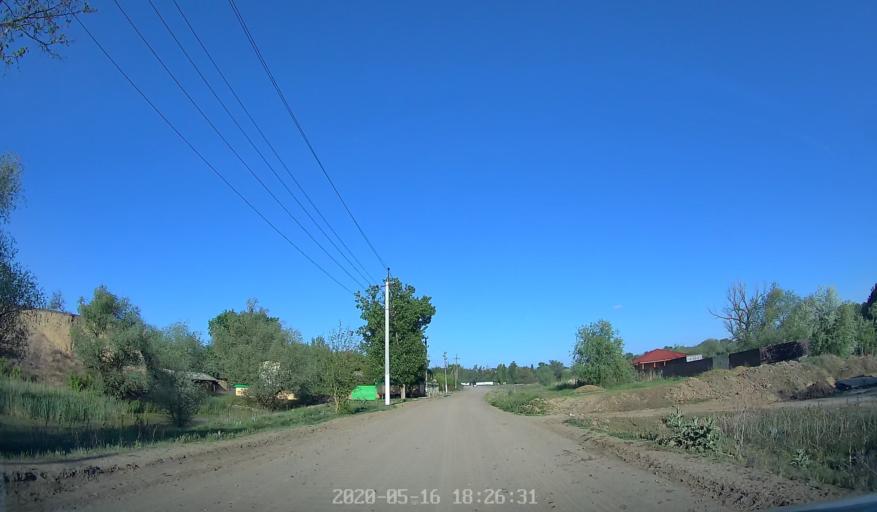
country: MD
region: Telenesti
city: Dnestrovsc
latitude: 46.5467
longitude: 30.0042
